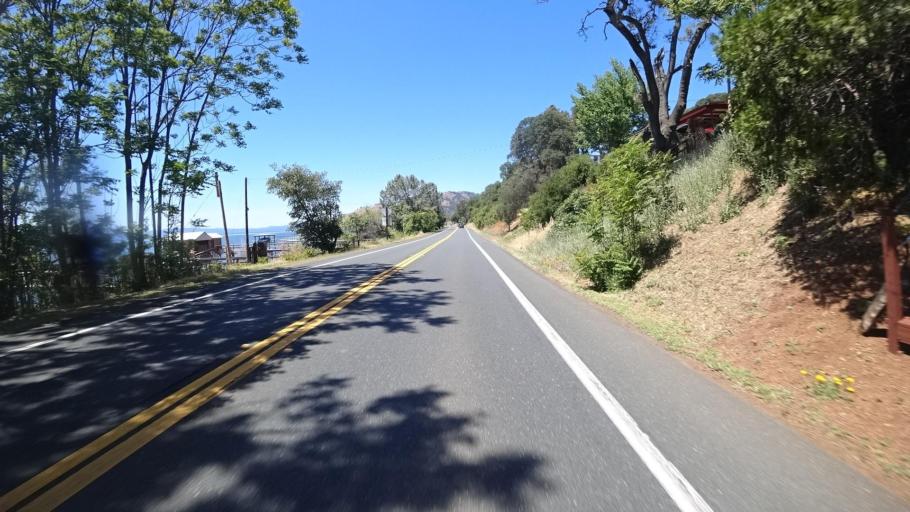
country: US
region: California
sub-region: Lake County
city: Soda Bay
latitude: 39.0274
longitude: -122.7353
